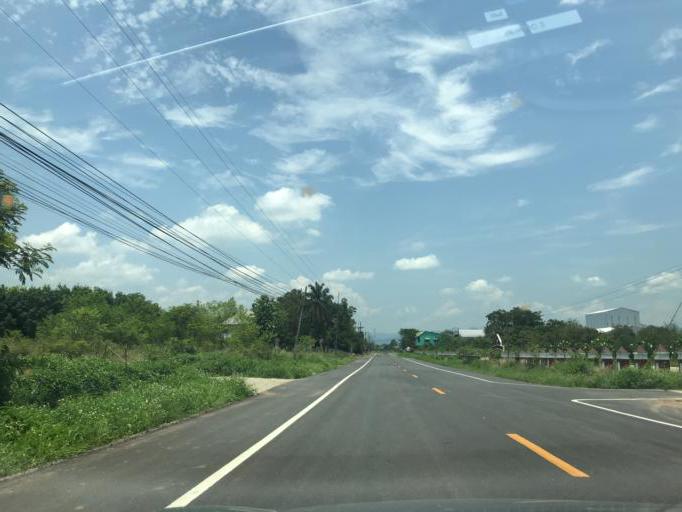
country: TH
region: Phayao
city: Phu Sang
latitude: 19.5871
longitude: 100.3105
